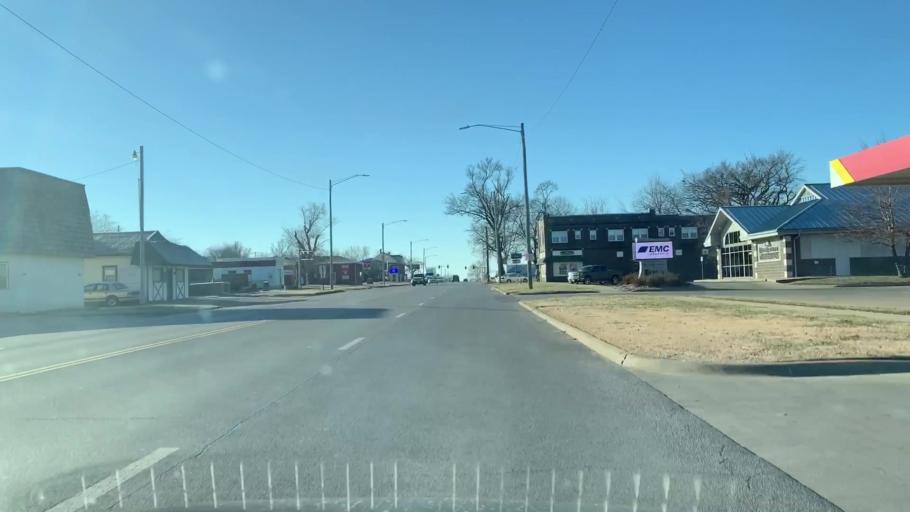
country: US
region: Kansas
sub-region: Crawford County
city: Pittsburg
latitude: 37.4031
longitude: -94.7050
